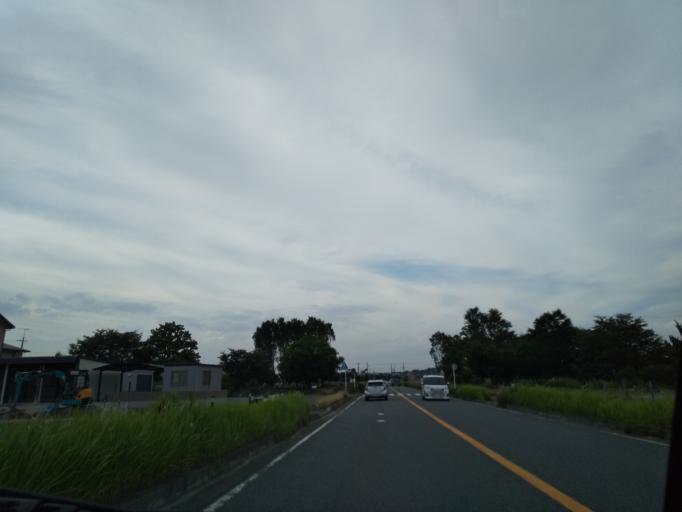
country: JP
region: Kanagawa
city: Zama
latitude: 35.4741
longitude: 139.3583
